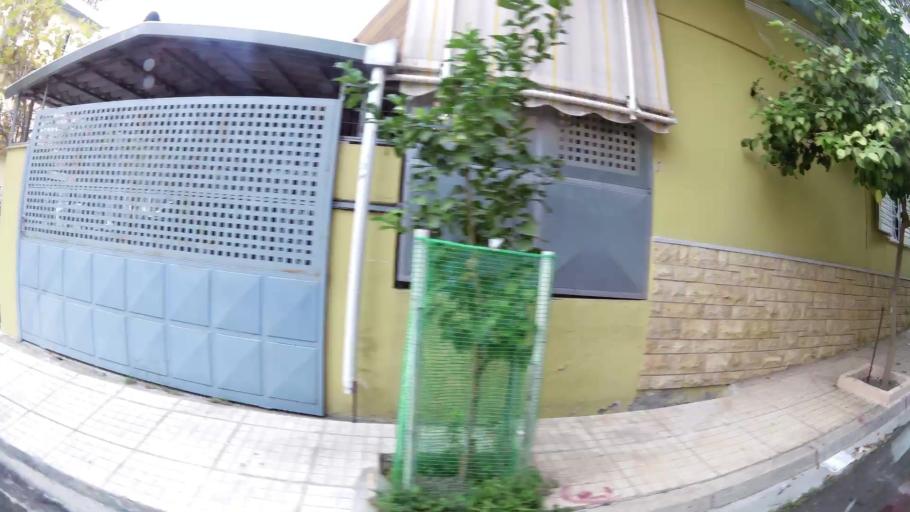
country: GR
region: Attica
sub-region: Nomarchia Athinas
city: Chaidari
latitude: 38.0112
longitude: 23.6718
